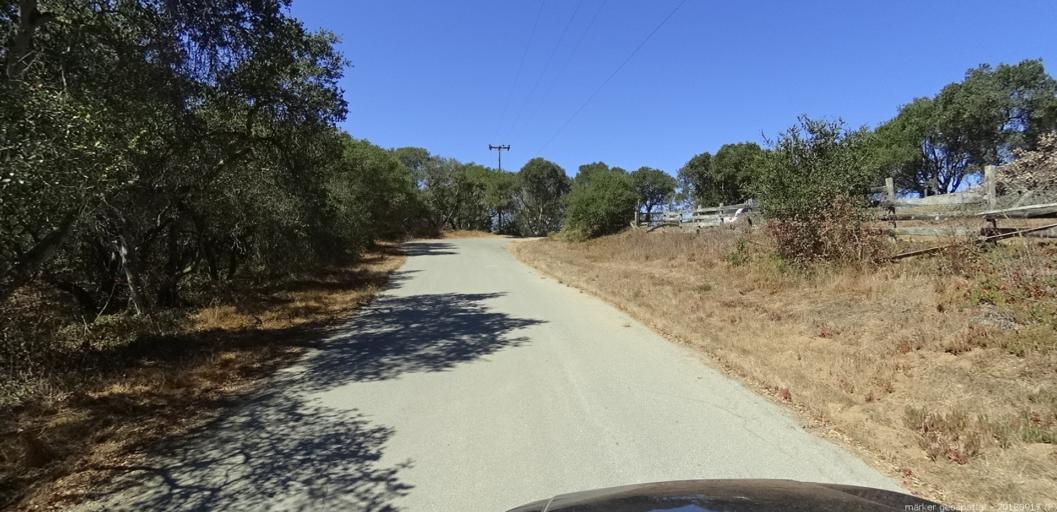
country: US
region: California
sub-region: San Benito County
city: Aromas
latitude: 36.8342
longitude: -121.6496
